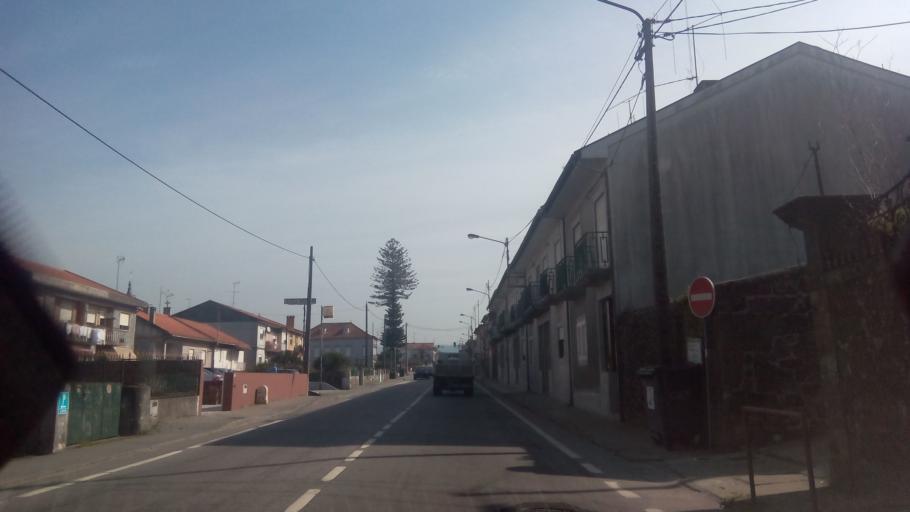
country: PT
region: Viana do Castelo
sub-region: Viana do Castelo
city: Darque
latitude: 41.6829
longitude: -8.7906
